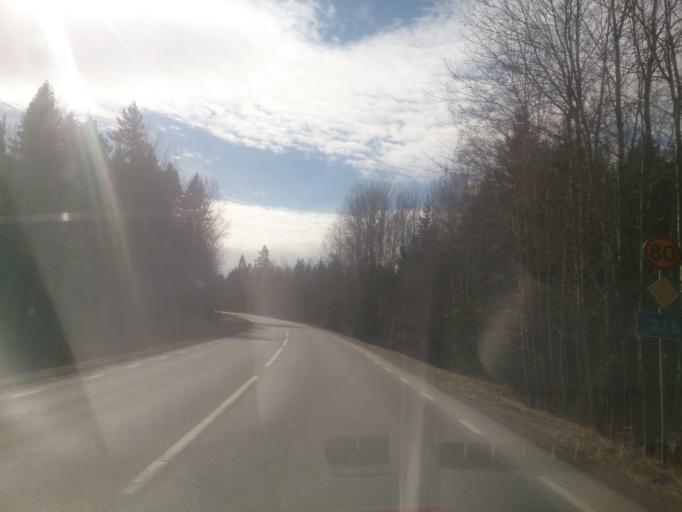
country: SE
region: OEstergoetland
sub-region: Finspangs Kommun
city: Finspang
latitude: 58.6176
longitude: 15.8117
